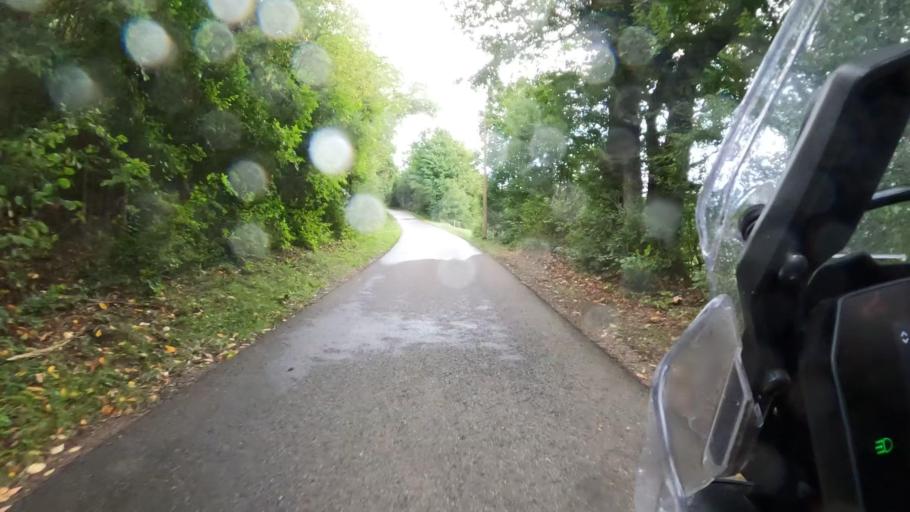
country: DE
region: Baden-Wuerttemberg
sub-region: Freiburg Region
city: Eggingen
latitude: 47.6703
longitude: 8.4022
